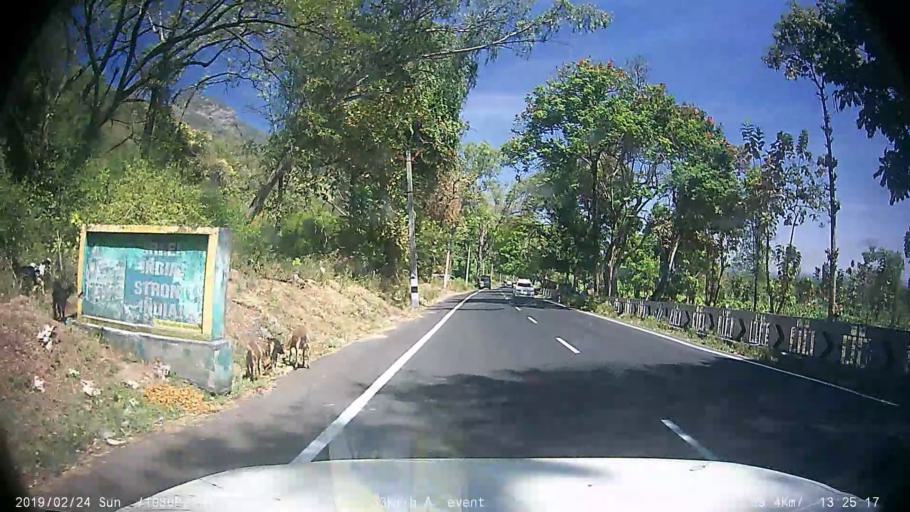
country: IN
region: Tamil Nadu
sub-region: Coimbatore
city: Mettupalayam
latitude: 11.3372
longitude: 76.8699
